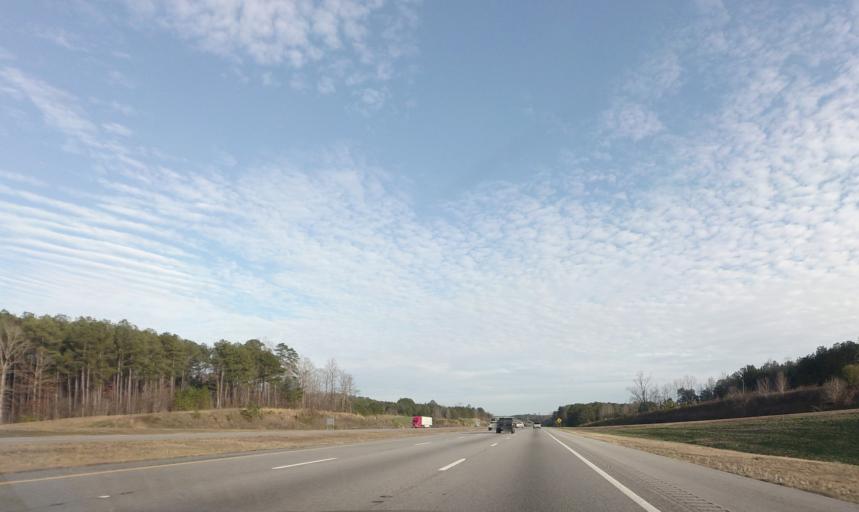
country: US
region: Alabama
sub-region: Walker County
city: Cordova
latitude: 33.7184
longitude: -87.1777
